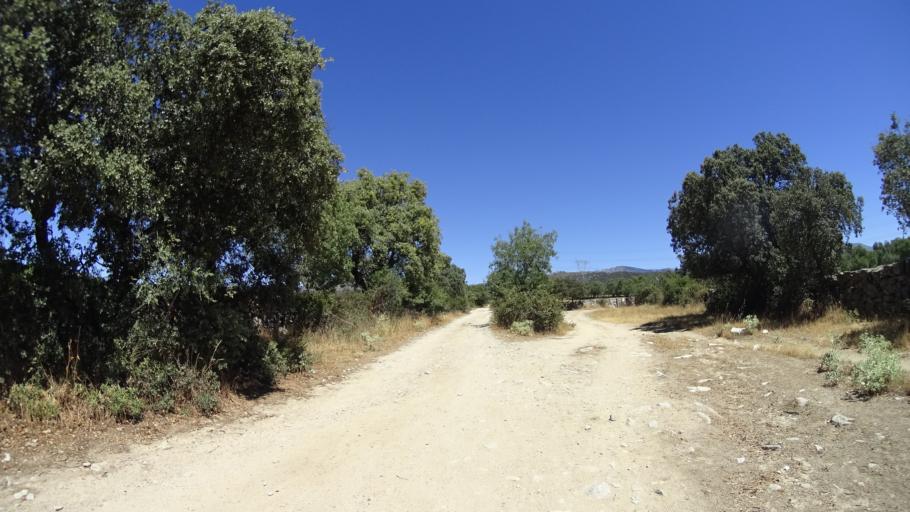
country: ES
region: Madrid
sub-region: Provincia de Madrid
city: Alpedrete
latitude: 40.6759
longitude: -4.0387
